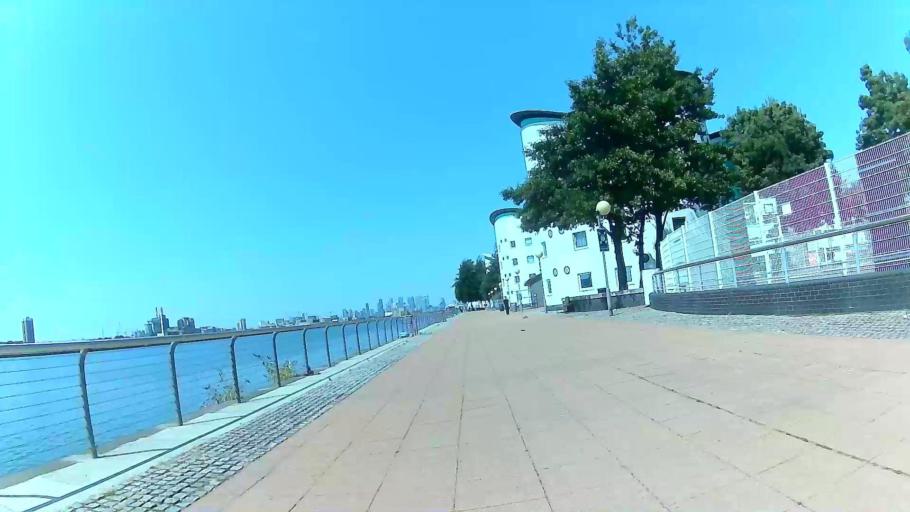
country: GB
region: England
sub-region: Greater London
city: Woolwich
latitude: 51.5068
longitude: 0.0664
